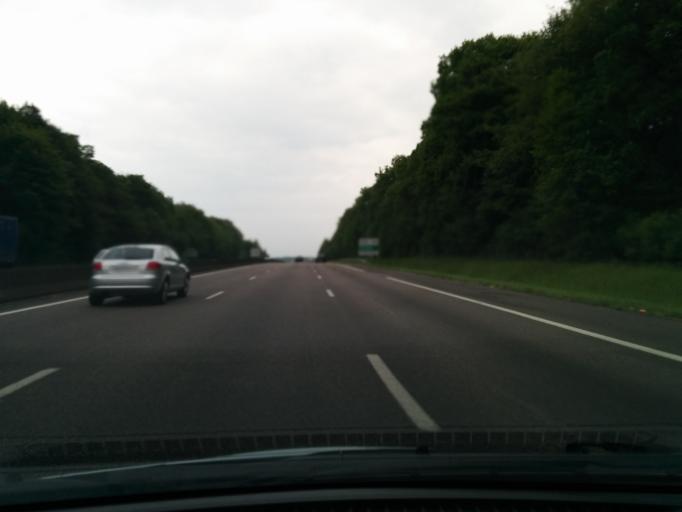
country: FR
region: Ile-de-France
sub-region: Departement des Yvelines
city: Rosny-sur-Seine
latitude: 49.0052
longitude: 1.6027
